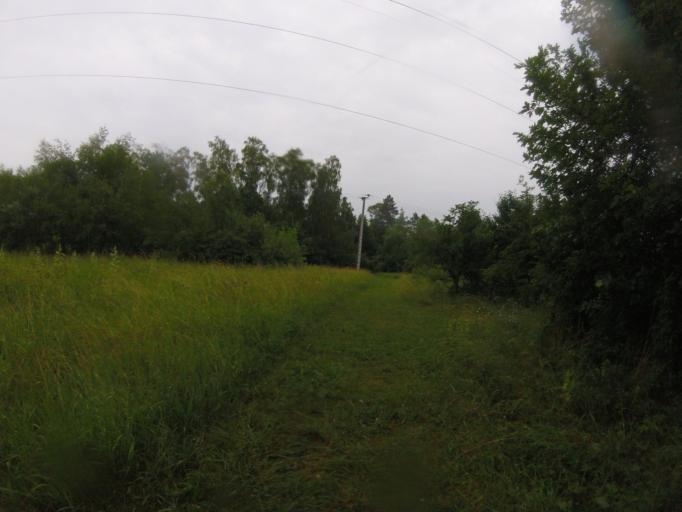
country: HU
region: Budapest
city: Budapest XXIII. keruelet
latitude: 47.3998
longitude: 19.1587
